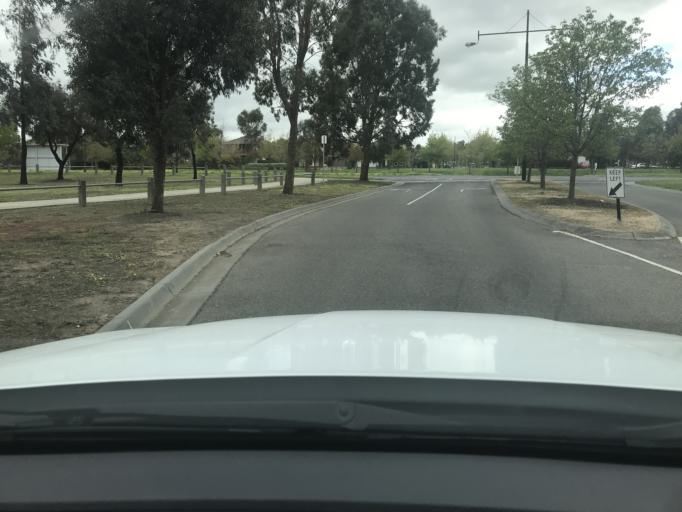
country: AU
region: Victoria
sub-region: Hume
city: Craigieburn
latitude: -37.5767
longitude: 144.9267
